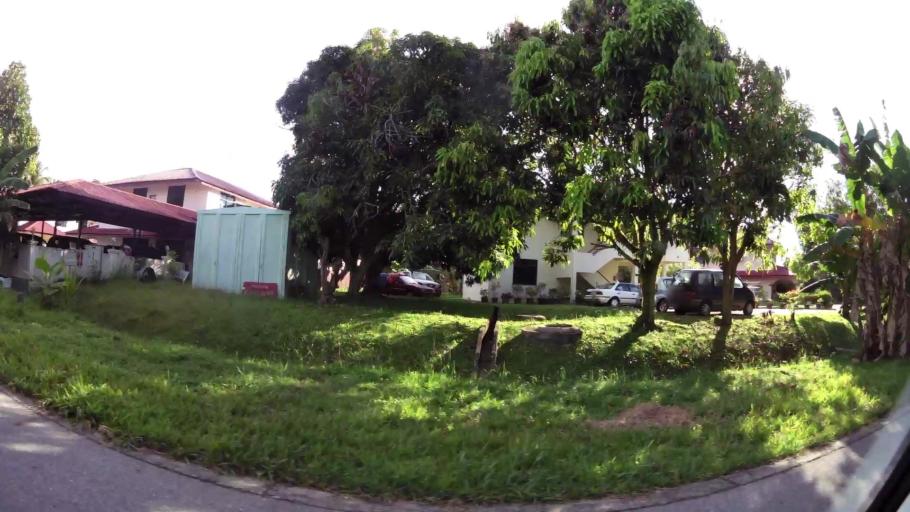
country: BN
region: Brunei and Muara
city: Bandar Seri Begawan
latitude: 4.9851
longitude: 114.9682
